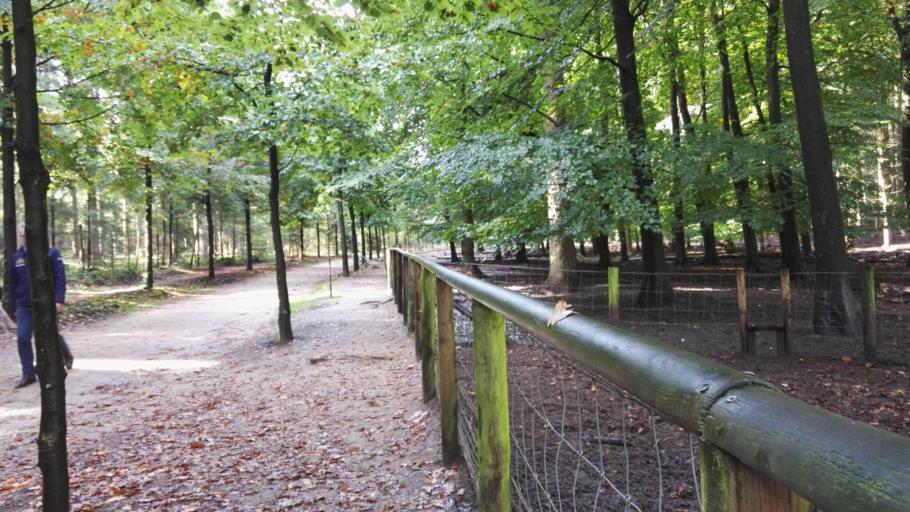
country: NL
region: Gelderland
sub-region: Gemeente Apeldoorn
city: Apeldoorn
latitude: 52.2101
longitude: 5.9202
